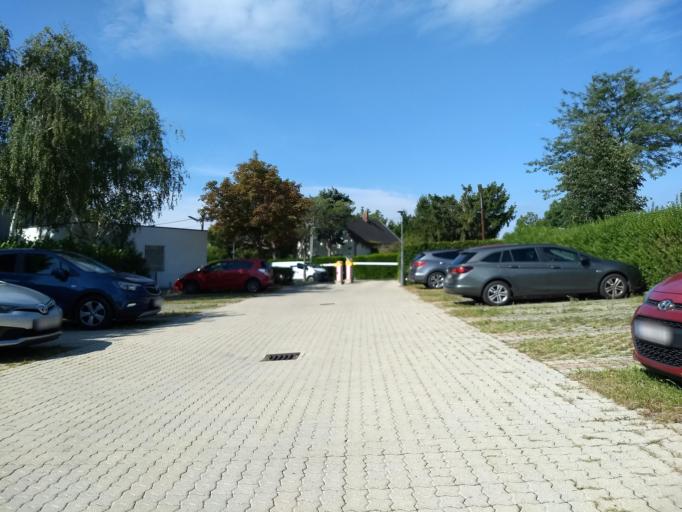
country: AT
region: Lower Austria
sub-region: Politischer Bezirk Ganserndorf
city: Aderklaa
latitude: 48.2335
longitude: 16.4935
